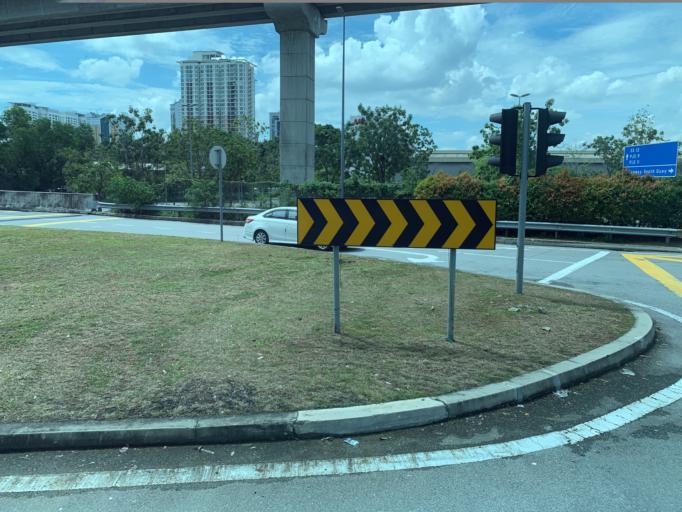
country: MY
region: Selangor
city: Subang Jaya
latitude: 3.0639
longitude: 101.5990
